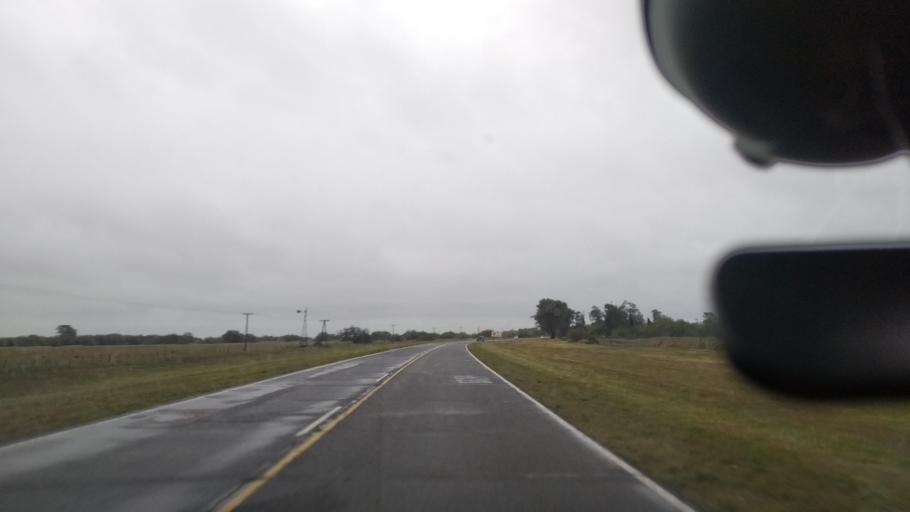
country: AR
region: Buenos Aires
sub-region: Partido de Castelli
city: Castelli
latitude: -36.0294
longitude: -57.4478
